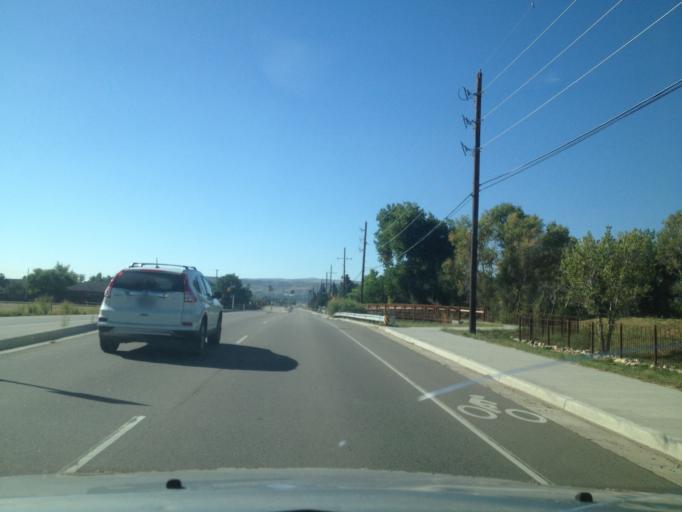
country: US
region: Colorado
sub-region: Jefferson County
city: Applewood
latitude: 39.7924
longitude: -105.1746
